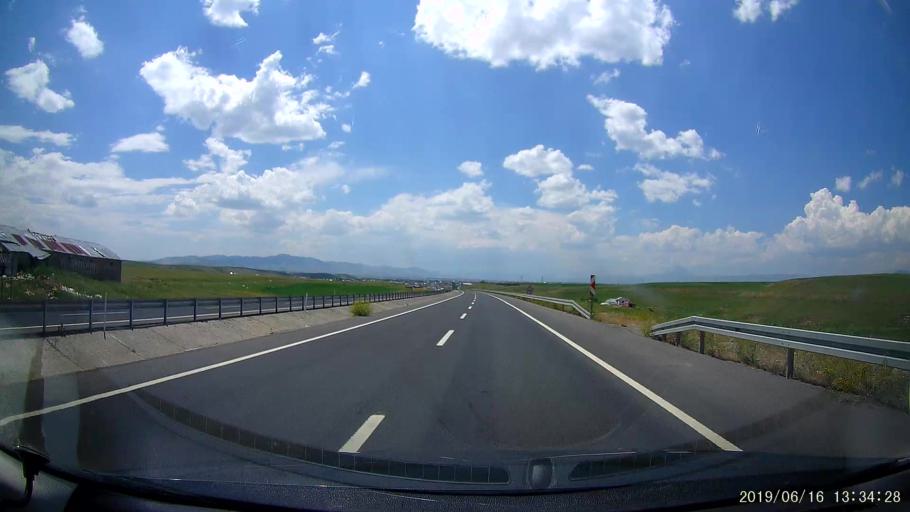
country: TR
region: Agri
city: Agri
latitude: 39.7128
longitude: 43.1256
